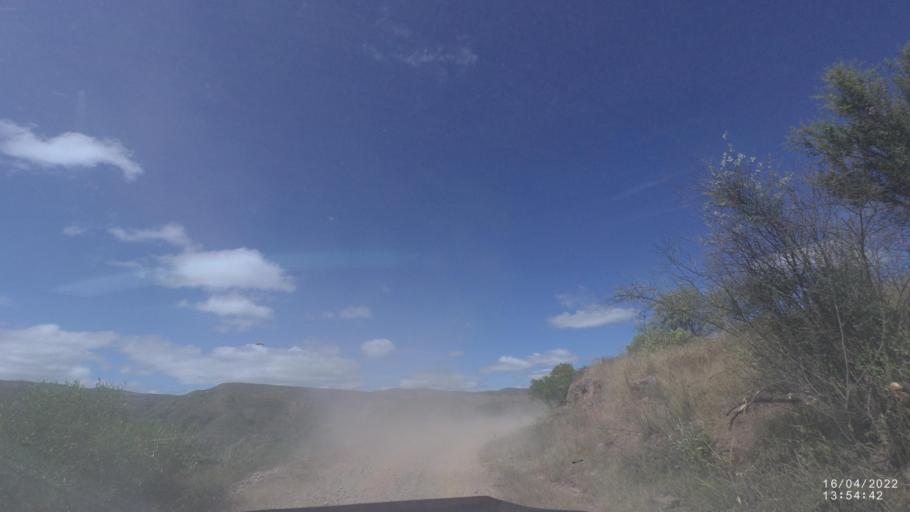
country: BO
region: Cochabamba
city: Mizque
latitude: -18.0261
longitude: -65.5639
